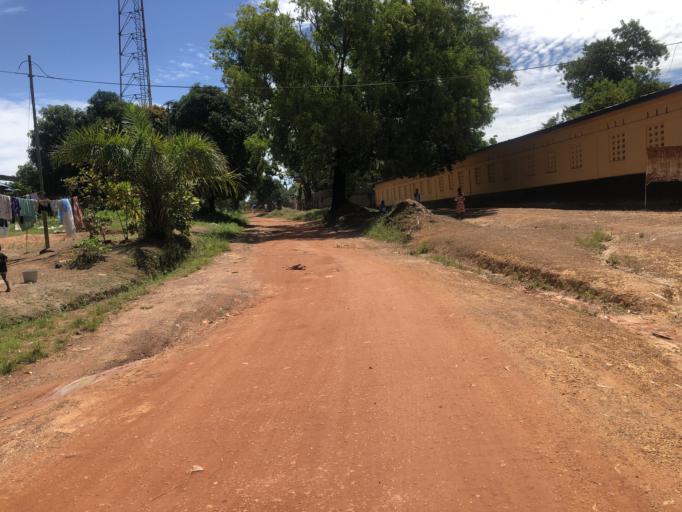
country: SL
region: Eastern Province
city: Koidu
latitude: 8.6403
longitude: -10.9641
